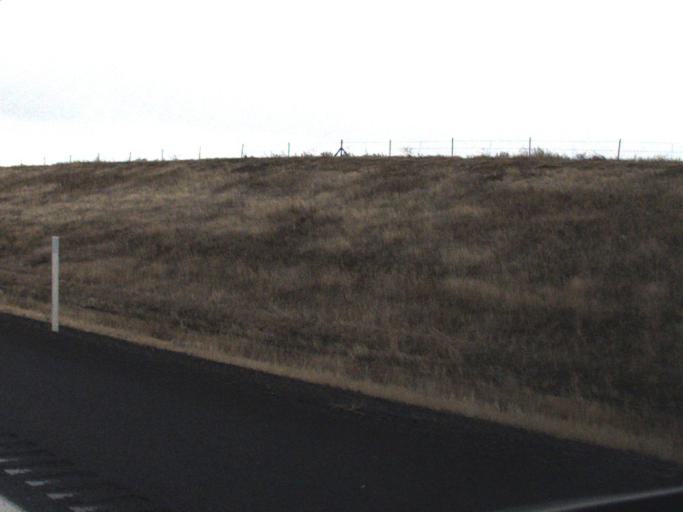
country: US
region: Washington
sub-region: Walla Walla County
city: Garrett
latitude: 46.0485
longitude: -118.4861
